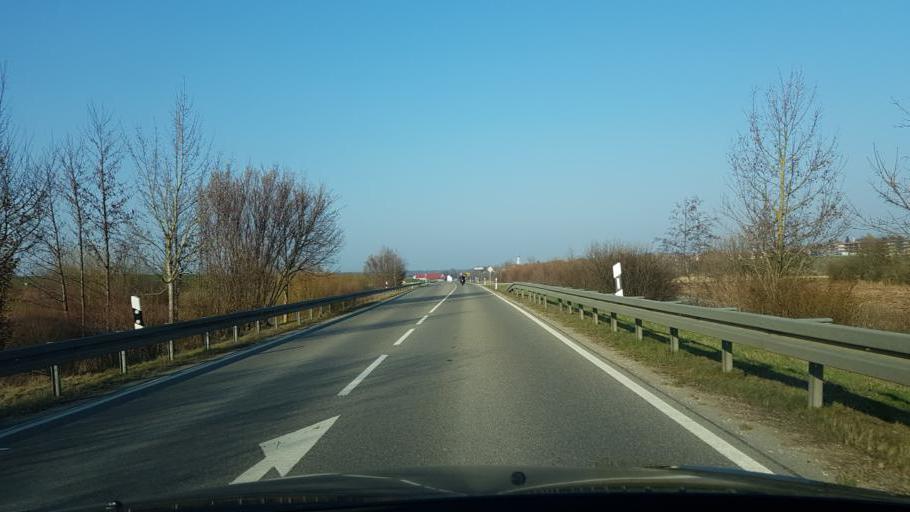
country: DE
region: Bavaria
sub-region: Upper Bavaria
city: Odelzhausen
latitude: 48.3015
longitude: 11.1807
